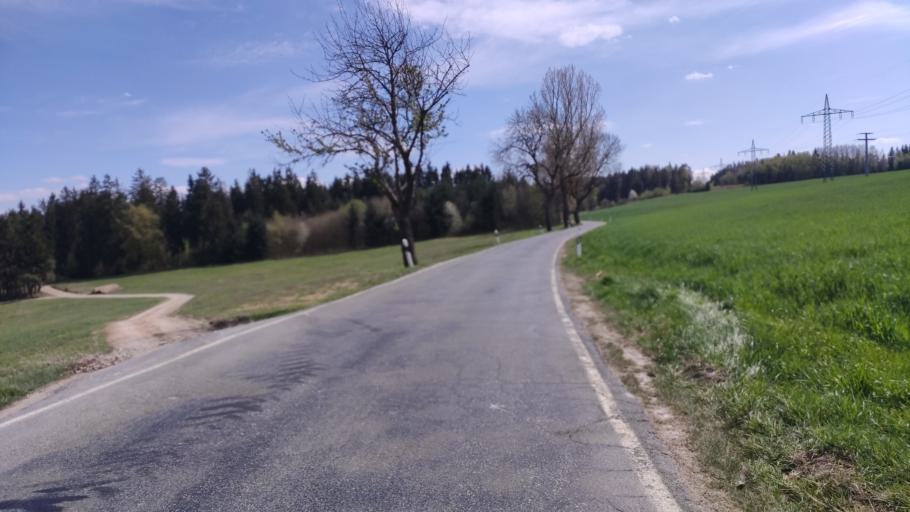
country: DE
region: Thuringia
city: Leutenberg
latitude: 50.5081
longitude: 11.4521
